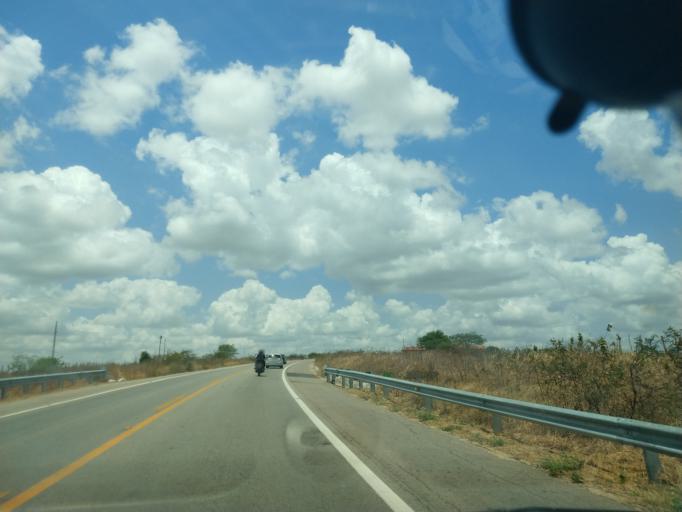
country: BR
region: Rio Grande do Norte
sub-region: Tangara
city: Tangara
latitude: -6.1878
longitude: -35.7796
